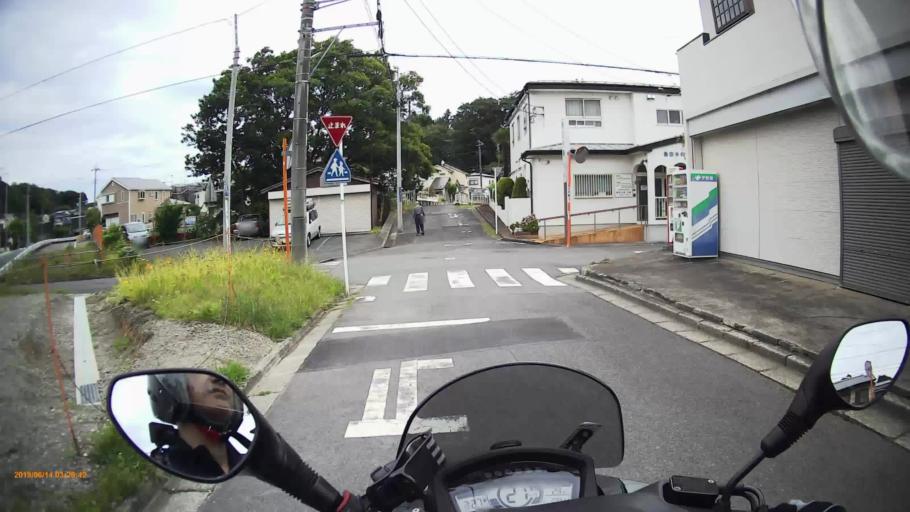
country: JP
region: Kanagawa
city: Fujisawa
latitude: 35.4112
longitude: 139.4529
